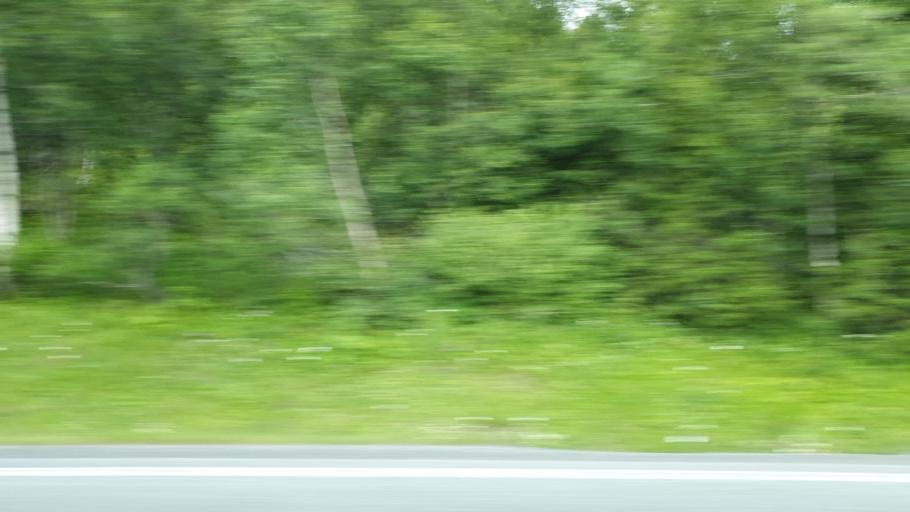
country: NO
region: Sor-Trondelag
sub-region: Rennebu
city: Berkak
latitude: 62.8603
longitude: 10.0211
